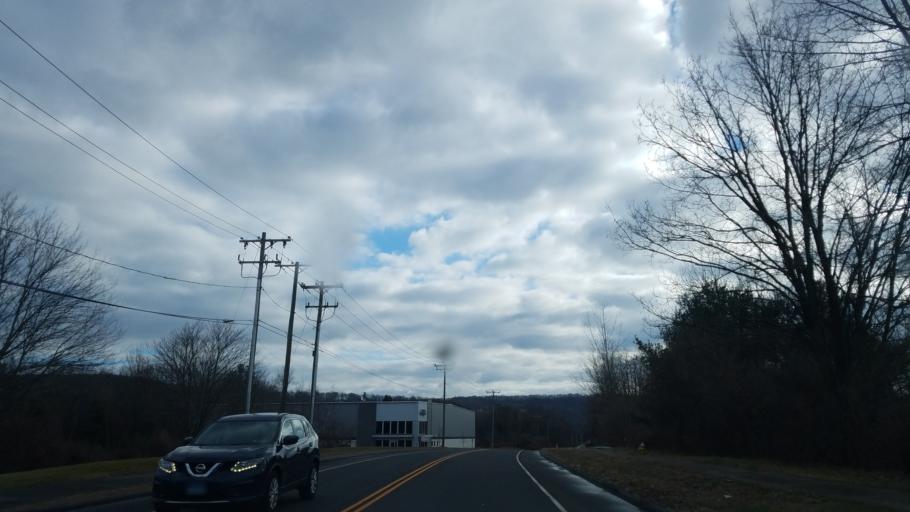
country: US
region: Connecticut
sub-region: Hartford County
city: Plainville
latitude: 41.6943
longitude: -72.8603
